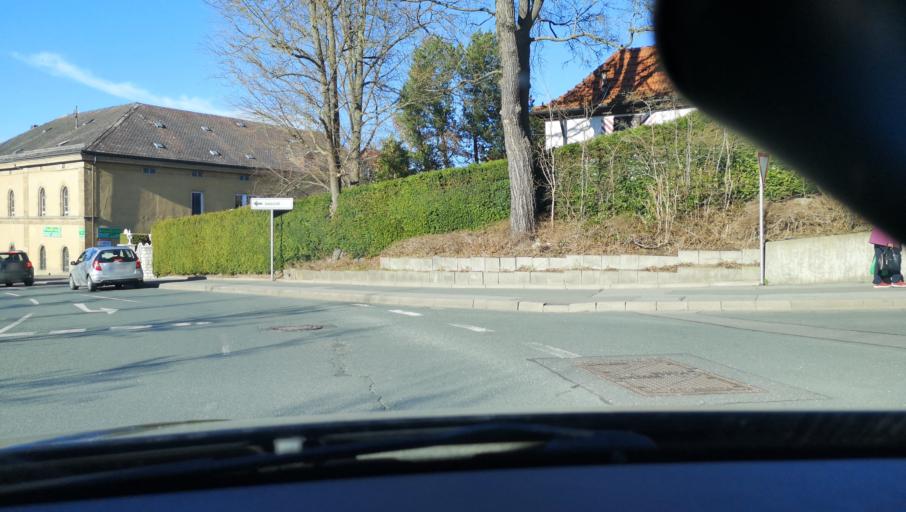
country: DE
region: Bavaria
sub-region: Upper Franconia
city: Lichtenfels
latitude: 50.1462
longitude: 11.0669
